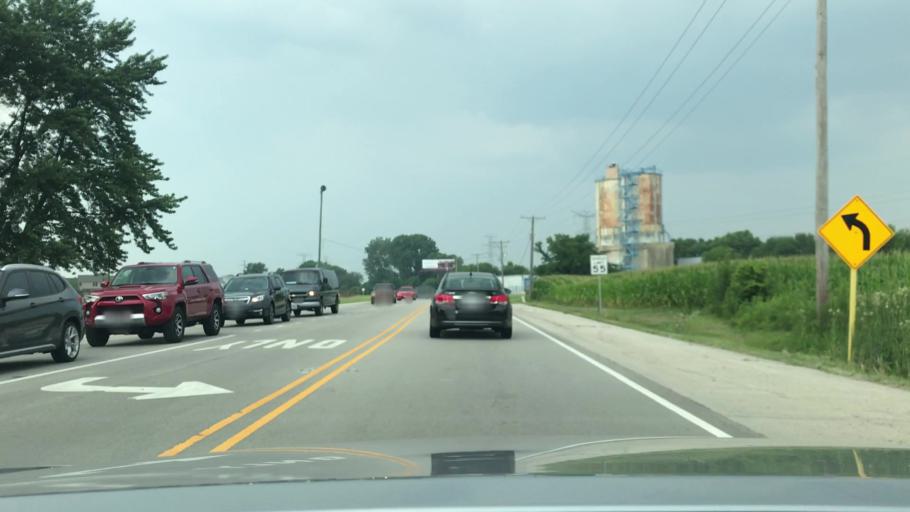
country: US
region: Illinois
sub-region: Will County
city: Plainfield
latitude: 41.6374
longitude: -88.2224
